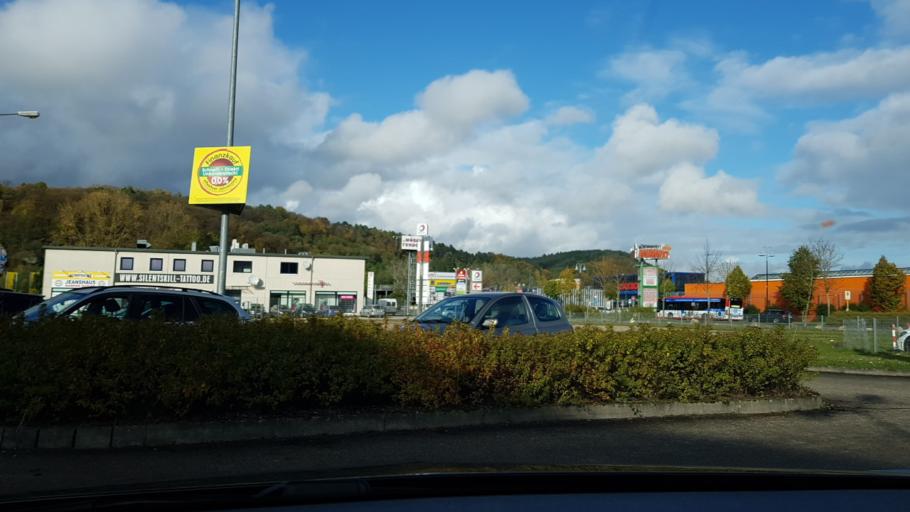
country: DE
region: Rheinland-Pfalz
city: Trier
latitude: 49.7709
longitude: 6.6590
